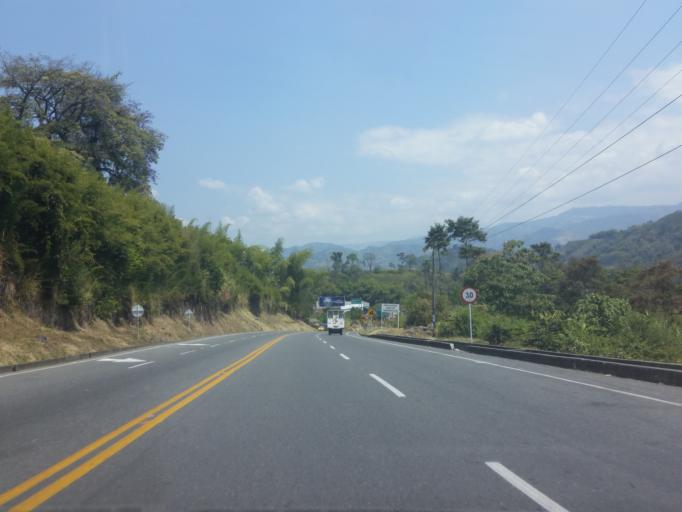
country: CO
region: Caldas
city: Chinchina
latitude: 4.9909
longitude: -75.6048
